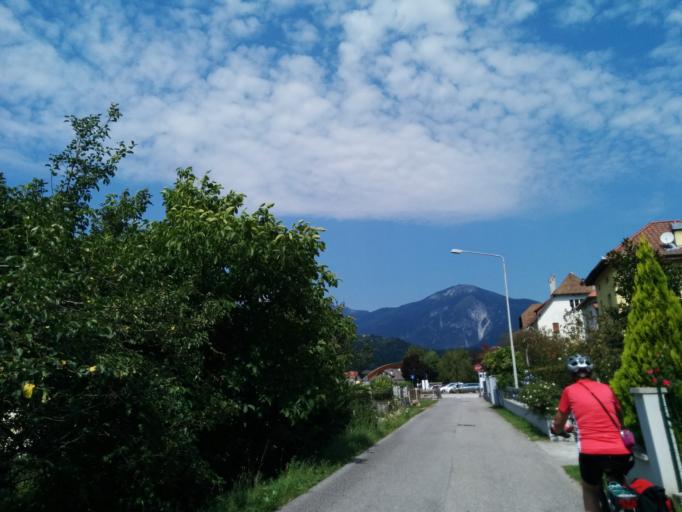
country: IT
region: Friuli Venezia Giulia
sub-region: Provincia di Udine
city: Ovaro
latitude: 46.4823
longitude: 12.8670
